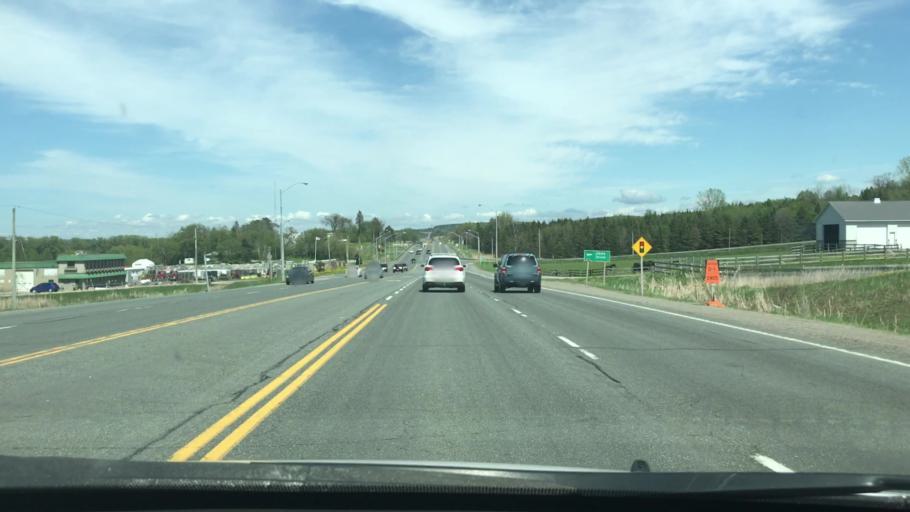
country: CA
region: Ontario
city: Bradford West Gwillimbury
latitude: 44.0316
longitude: -79.5832
